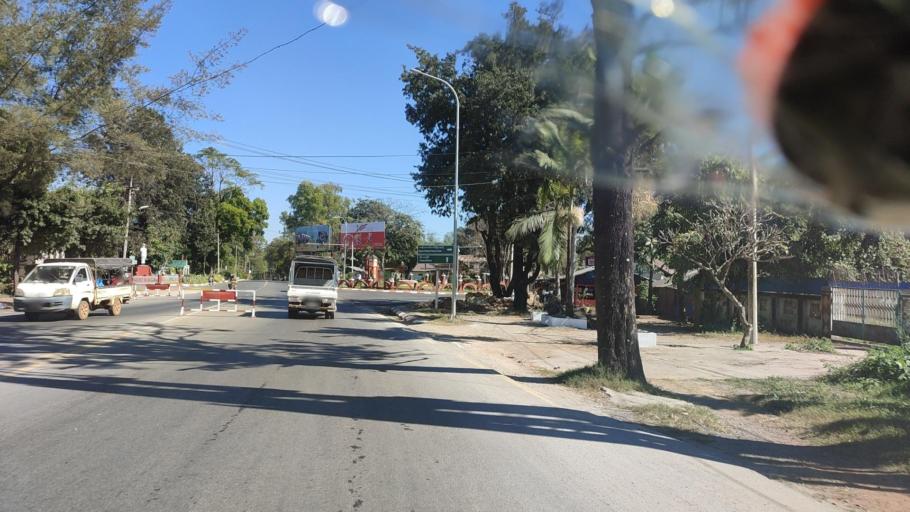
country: MM
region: Mandalay
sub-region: Pyin Oo Lwin District
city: Pyin Oo Lwin
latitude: 22.0138
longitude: 96.4465
